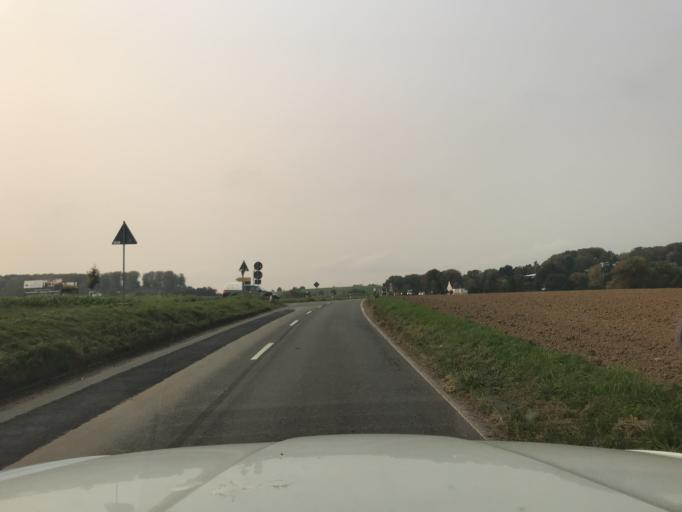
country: DE
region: North Rhine-Westphalia
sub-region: Regierungsbezirk Dusseldorf
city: Heiligenhaus
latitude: 51.3938
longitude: 6.9664
